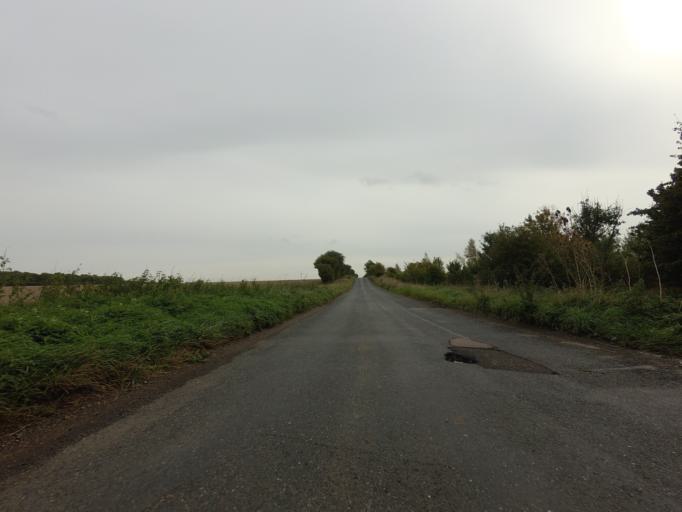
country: GB
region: England
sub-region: Hertfordshire
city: Reed
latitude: 51.9938
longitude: 0.0204
